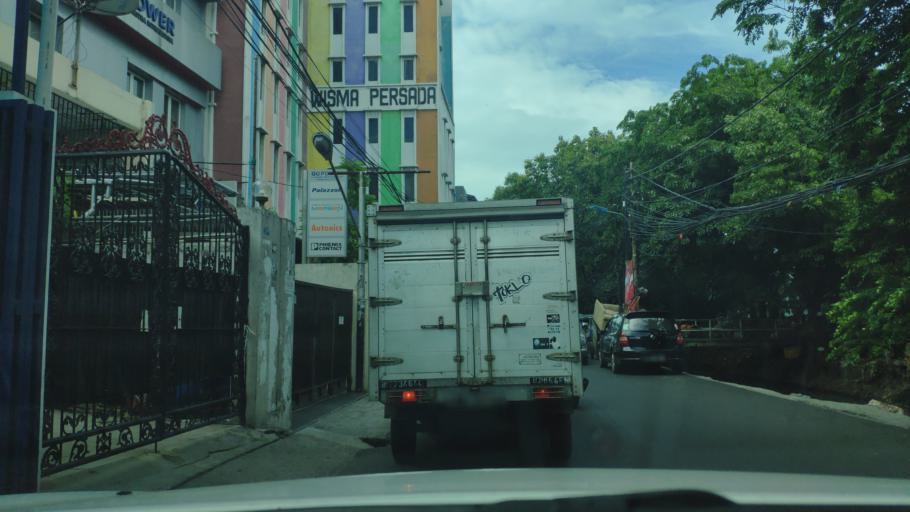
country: ID
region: Jakarta Raya
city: Jakarta
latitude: -6.1468
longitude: 106.8205
